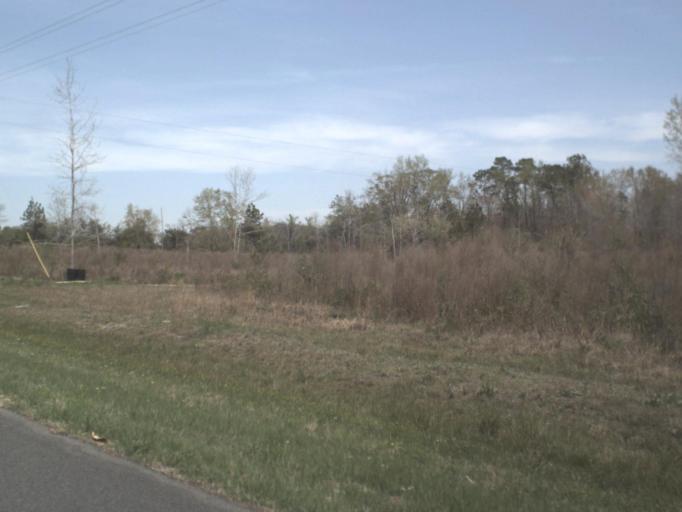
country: US
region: Alabama
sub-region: Geneva County
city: Geneva
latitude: 30.8810
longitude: -85.9494
